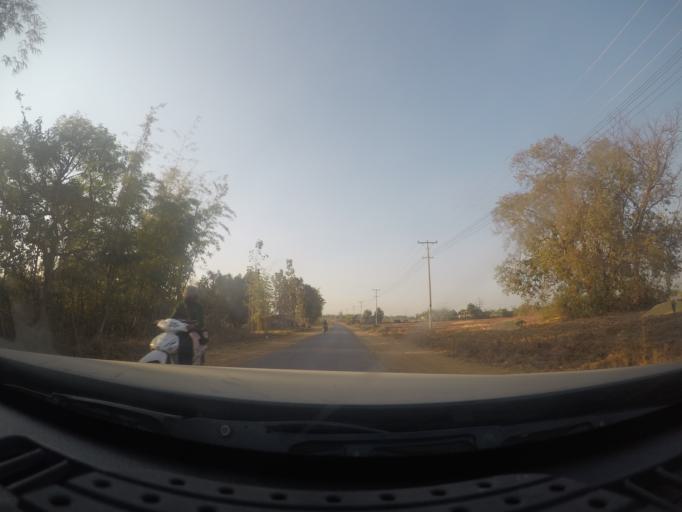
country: MM
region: Shan
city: Taunggyi
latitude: 20.4653
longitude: 97.1273
